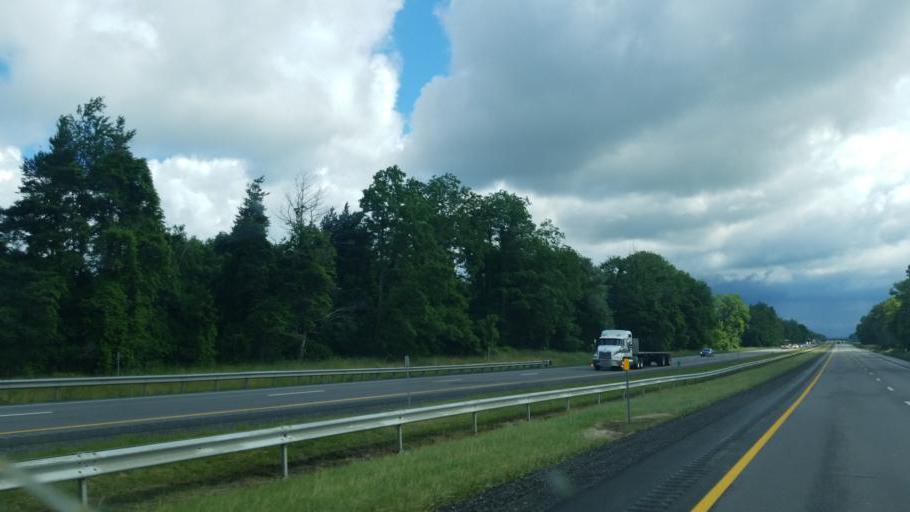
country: US
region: New York
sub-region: Chautauqua County
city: Silver Creek
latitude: 42.5316
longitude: -79.1317
